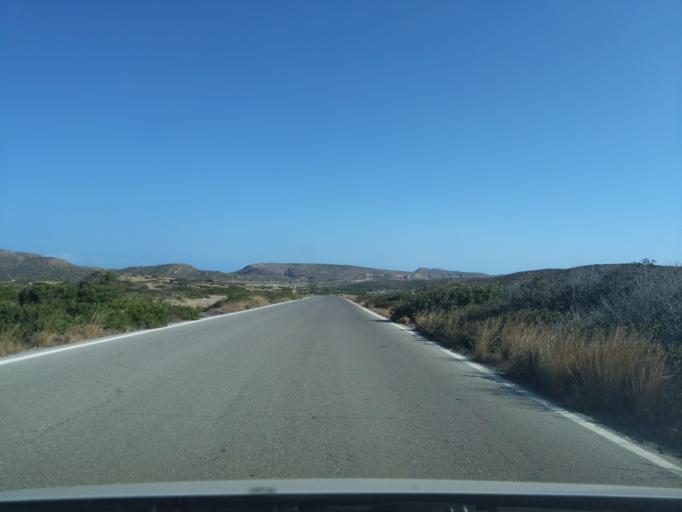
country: GR
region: Crete
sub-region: Nomos Lasithiou
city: Palekastro
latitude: 35.2440
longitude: 26.2487
